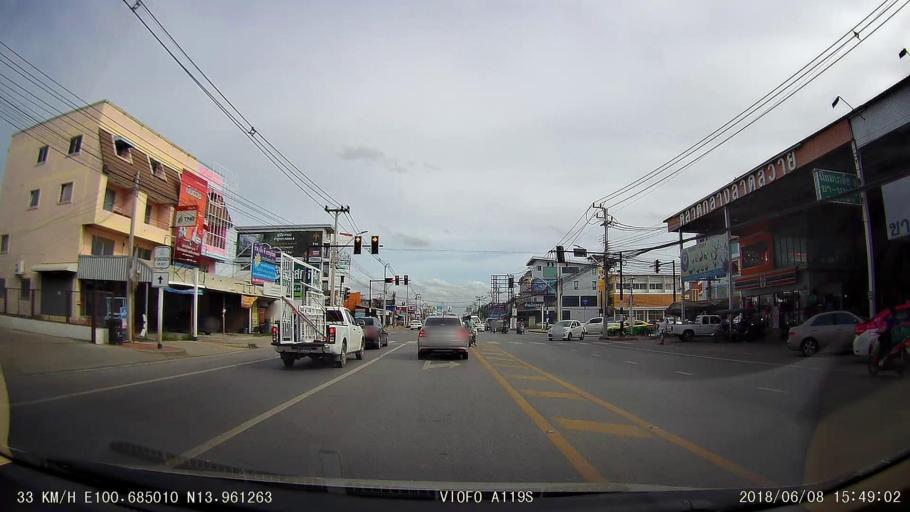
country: TH
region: Bangkok
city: Sai Mai
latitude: 13.9613
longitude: 100.6851
